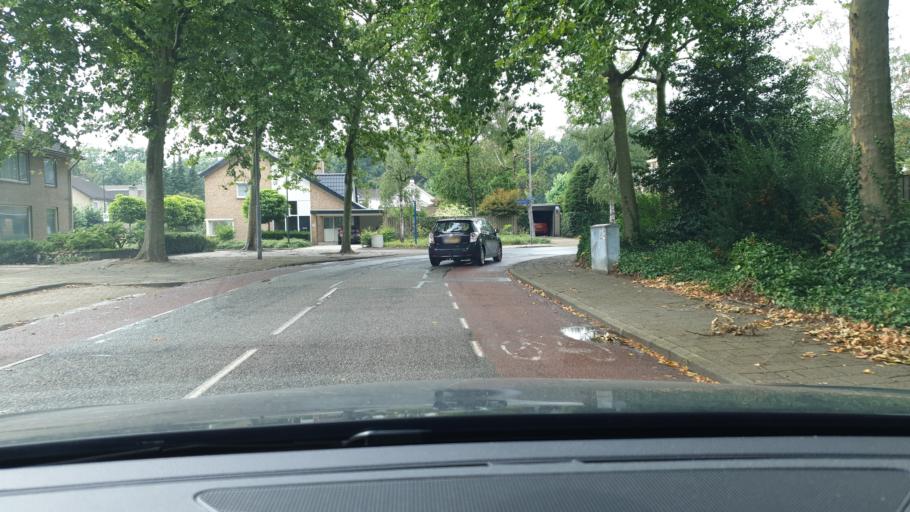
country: NL
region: North Brabant
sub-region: Gemeente Veldhoven
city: Oerle
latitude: 51.4154
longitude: 5.3856
